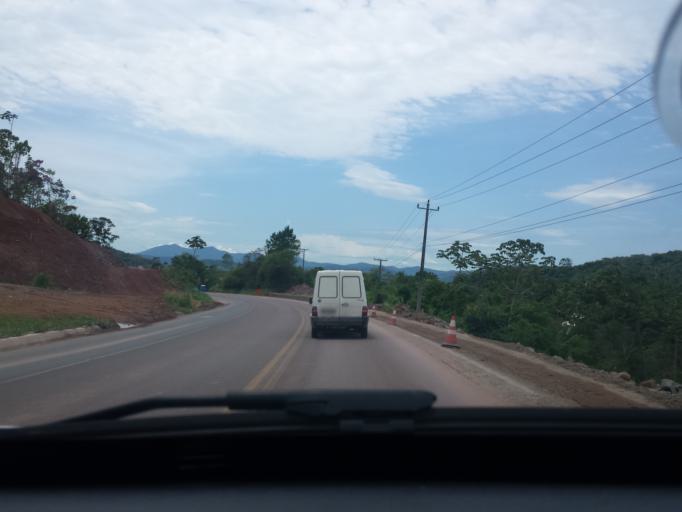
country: BR
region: Santa Catarina
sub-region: Gaspar
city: Gaspar
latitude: -26.8956
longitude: -48.9879
